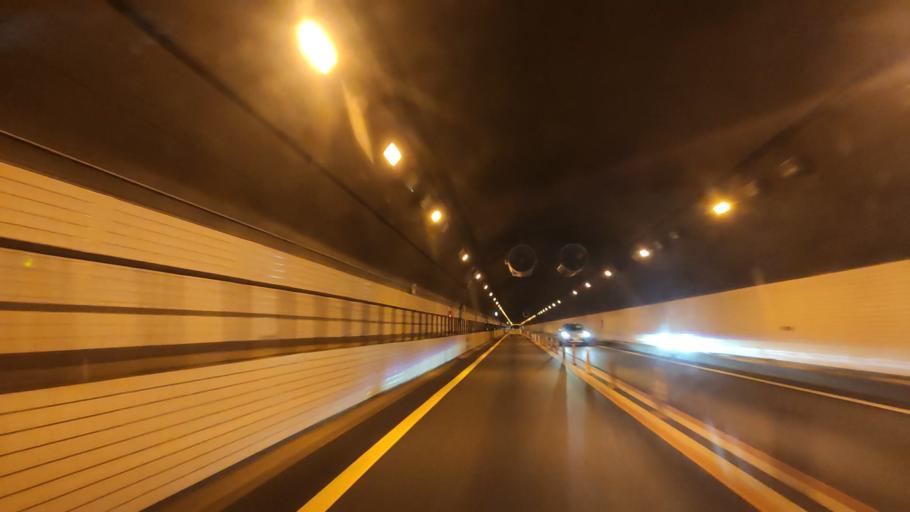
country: JP
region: Ehime
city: Kawanoecho
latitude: 34.0043
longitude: 133.6923
